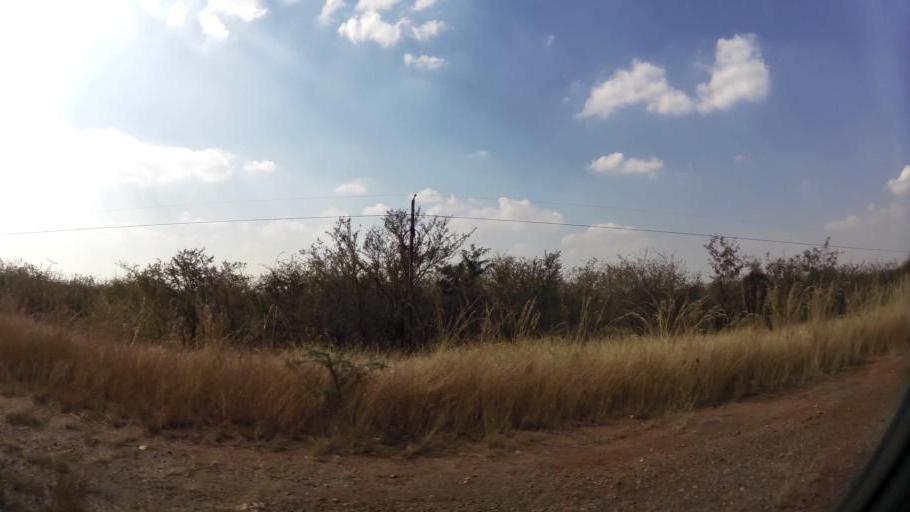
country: ZA
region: North-West
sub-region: Bojanala Platinum District Municipality
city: Rustenburg
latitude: -25.5323
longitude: 27.1169
